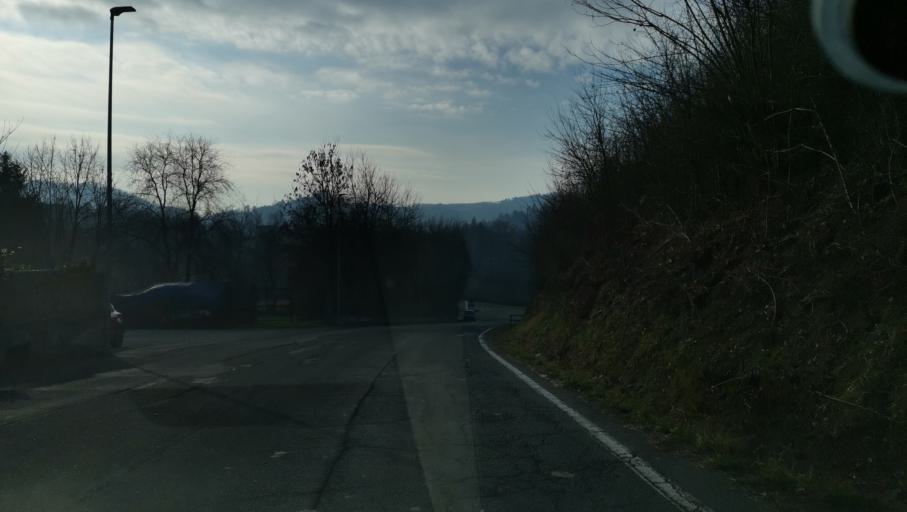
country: IT
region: Piedmont
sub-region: Provincia di Torino
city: Rivalba
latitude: 45.1130
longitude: 7.8866
